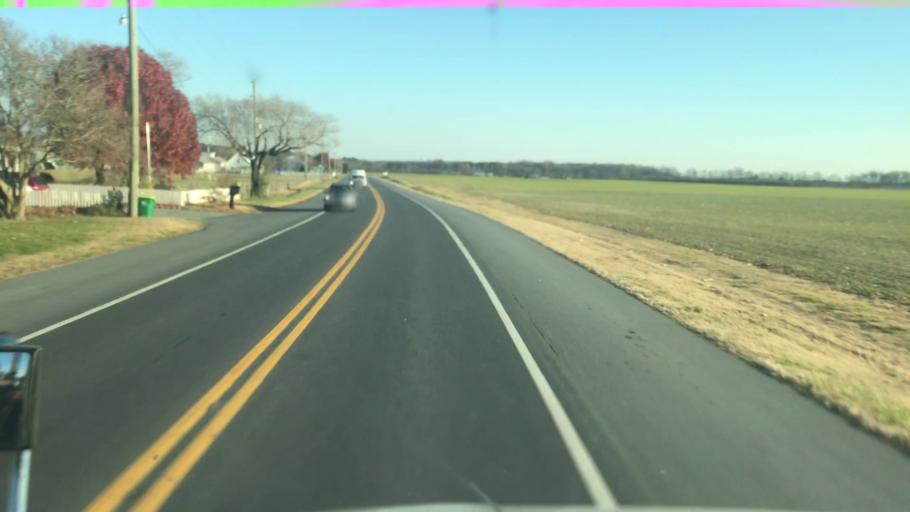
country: US
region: Delaware
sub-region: Sussex County
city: Bridgeville
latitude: 38.7899
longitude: -75.6879
